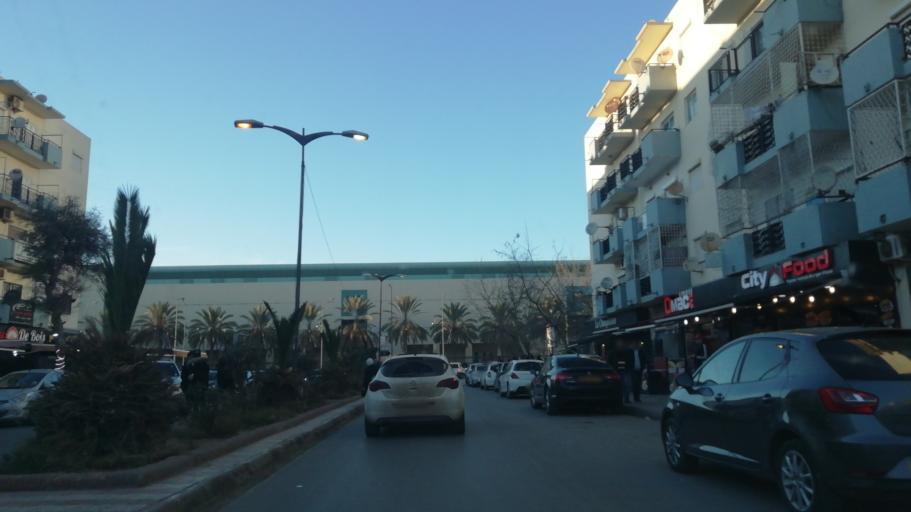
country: DZ
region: Oran
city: Bir el Djir
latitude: 35.7262
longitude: -0.5885
